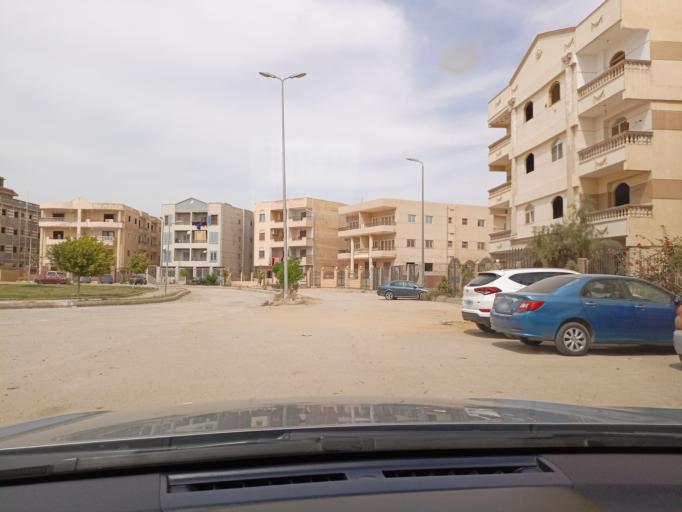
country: EG
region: Muhafazat al Qalyubiyah
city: Al Khankah
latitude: 30.2501
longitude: 31.5015
